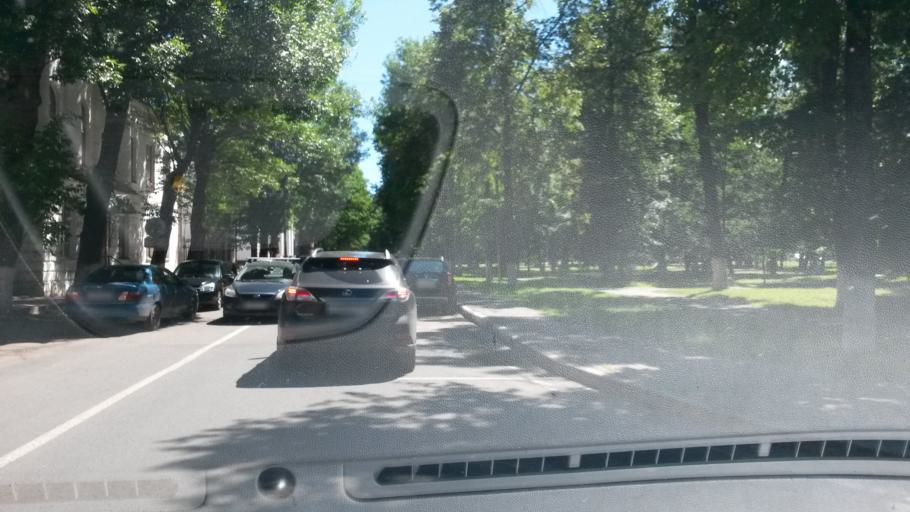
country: RU
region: Jaroslavl
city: Yaroslavl
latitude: 57.6264
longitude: 39.8963
